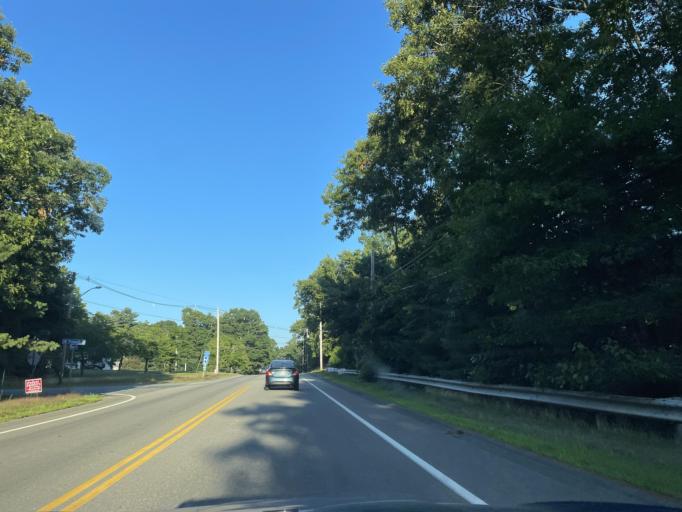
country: US
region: Massachusetts
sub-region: Plymouth County
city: Halifax
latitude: 41.9944
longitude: -70.8781
